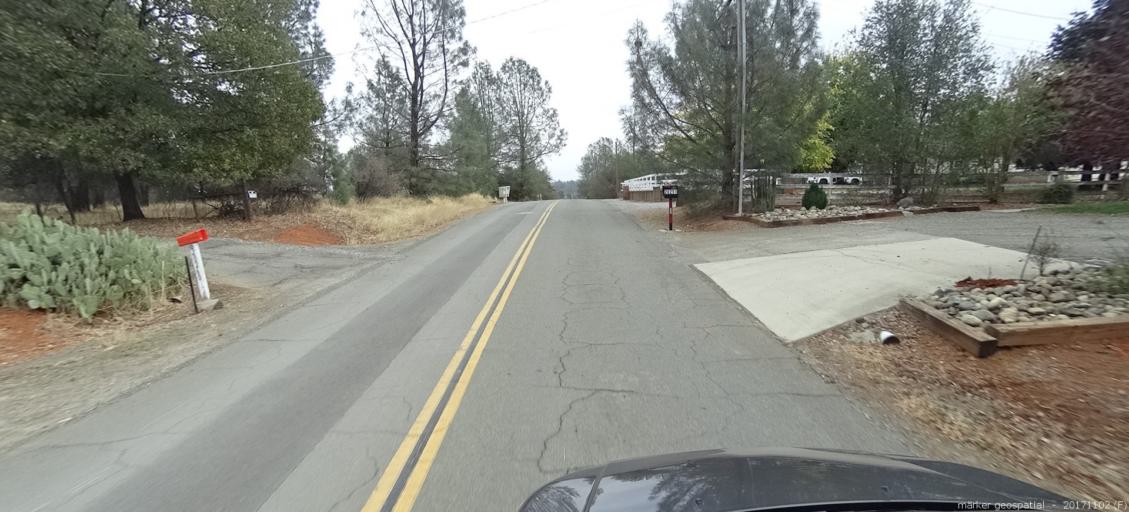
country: US
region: California
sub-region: Shasta County
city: Shasta Lake
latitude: 40.6510
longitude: -122.3072
